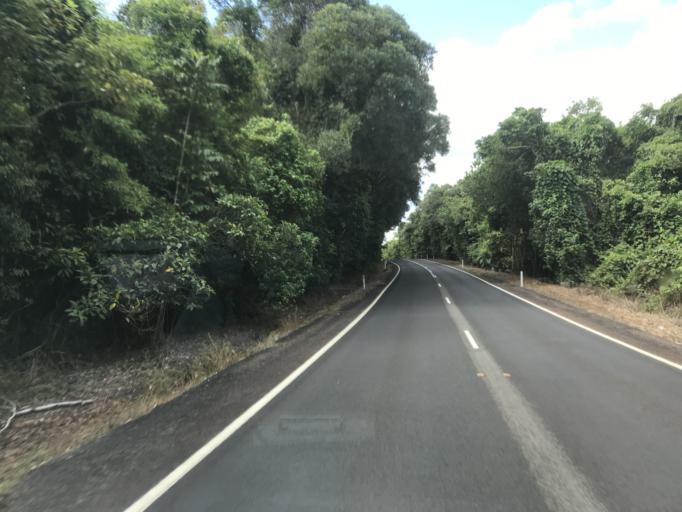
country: AU
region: Queensland
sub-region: Cassowary Coast
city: Innisfail
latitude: -17.8552
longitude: 146.0659
